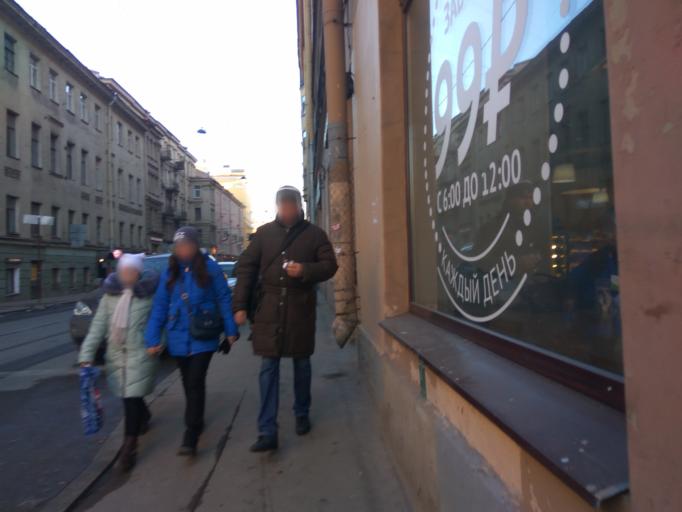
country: RU
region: St.-Petersburg
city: Saint Petersburg
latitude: 59.9282
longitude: 30.3158
